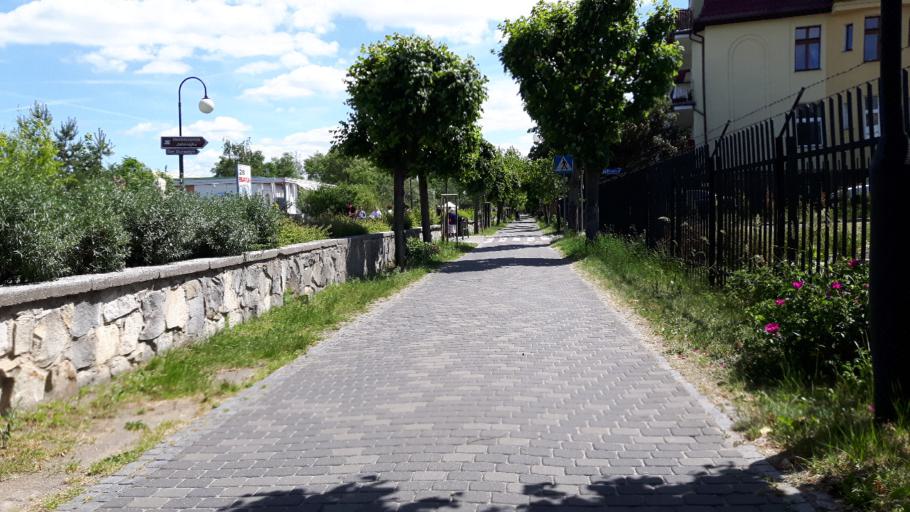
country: PL
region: Pomeranian Voivodeship
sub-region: Sopot
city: Sopot
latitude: 54.4410
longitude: 18.5755
